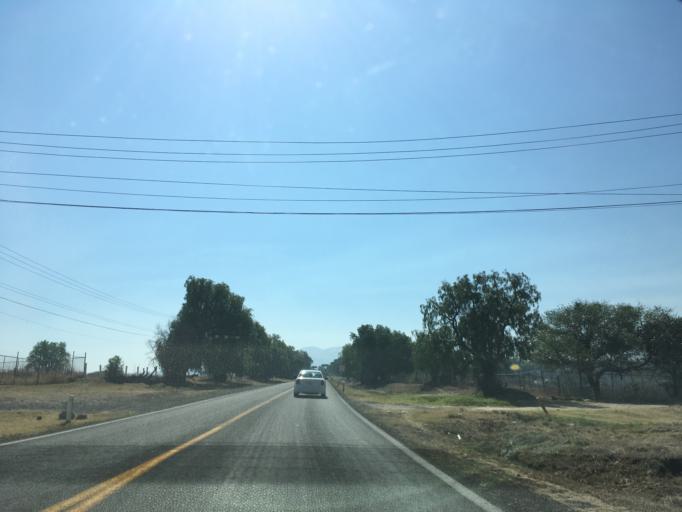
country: MX
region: Michoacan
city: Charo
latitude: 19.7469
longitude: -101.0576
